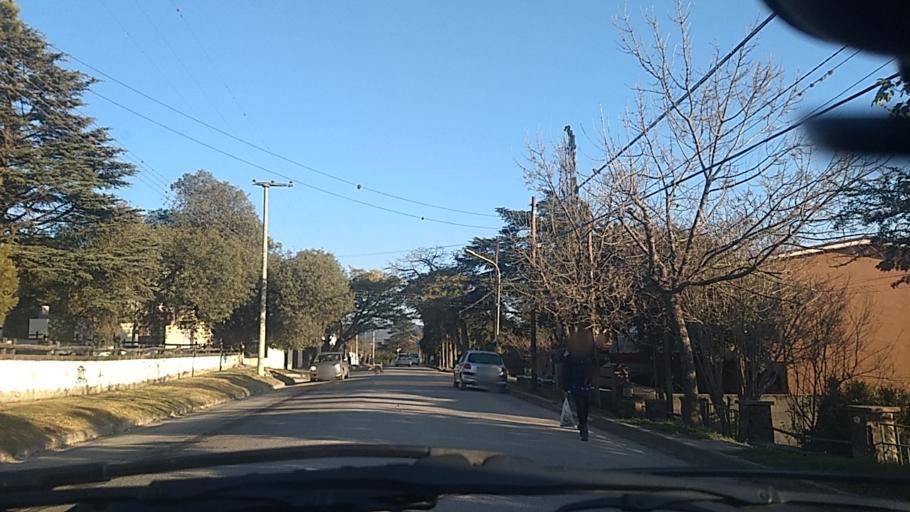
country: AR
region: Cordoba
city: Salsipuedes
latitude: -31.1400
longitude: -64.2888
